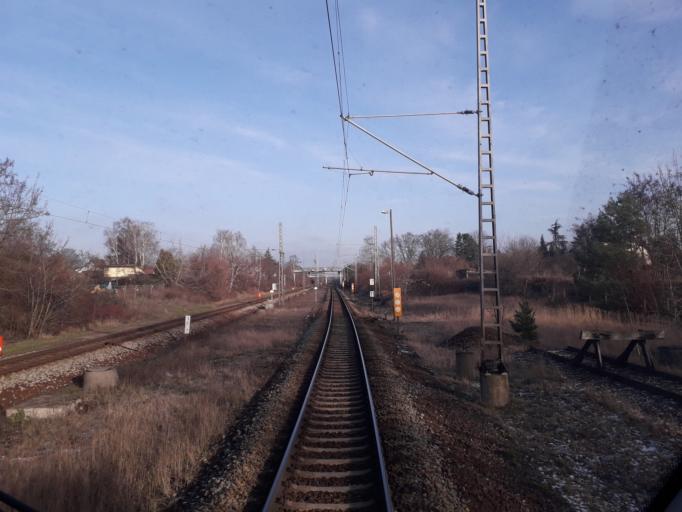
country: DE
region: Berlin
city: Altglienicke
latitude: 52.3978
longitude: 13.5266
